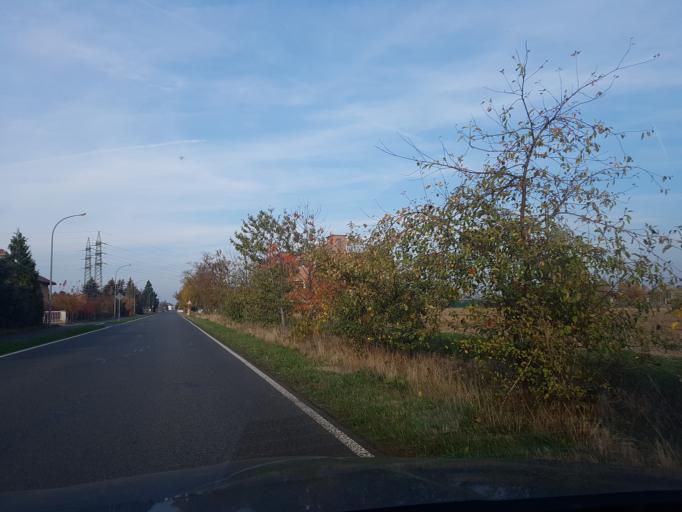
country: DE
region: Brandenburg
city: Falkenberg
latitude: 51.5688
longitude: 13.2292
